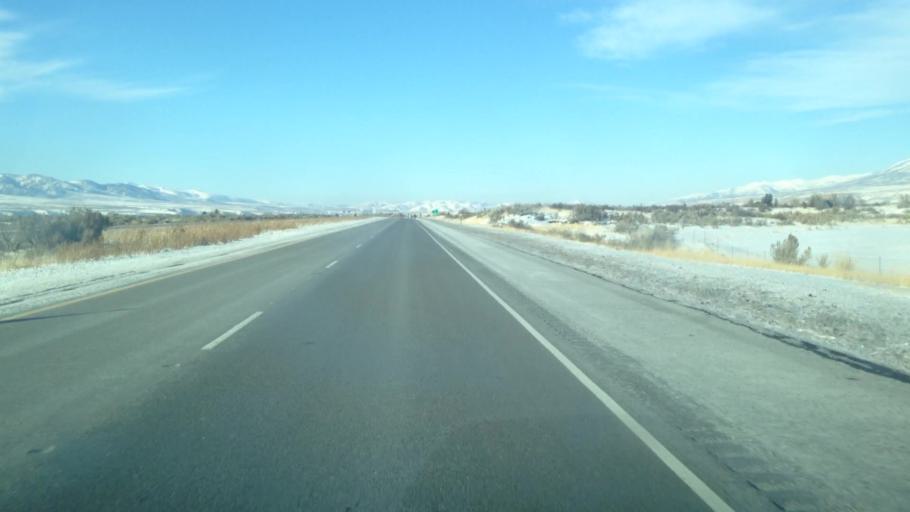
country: US
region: Idaho
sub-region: Bannock County
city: Pocatello
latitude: 42.6072
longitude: -112.1953
